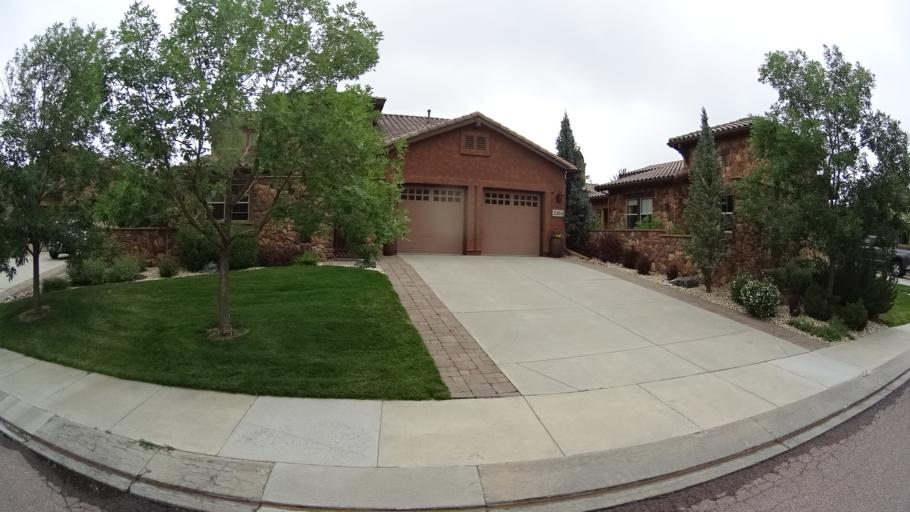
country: US
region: Colorado
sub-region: El Paso County
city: Gleneagle
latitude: 39.0222
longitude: -104.7854
